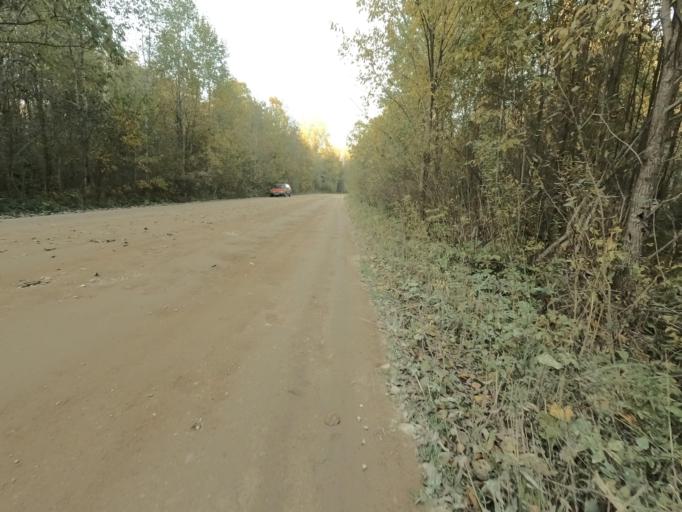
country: RU
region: Leningrad
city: Lyuban'
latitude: 58.9851
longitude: 31.0987
